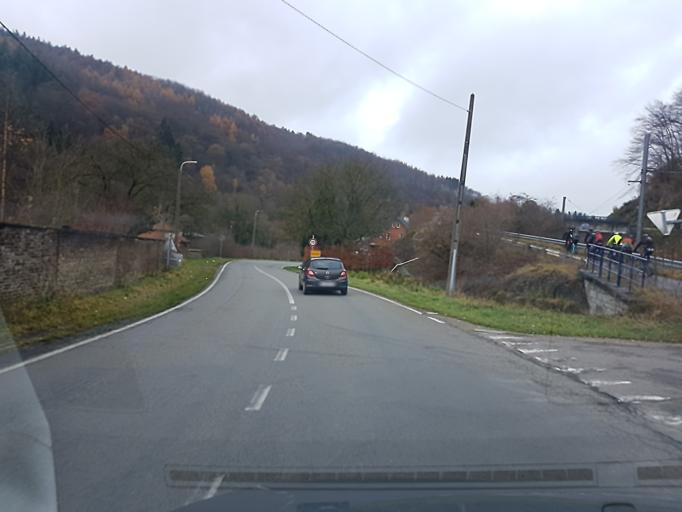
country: BE
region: Wallonia
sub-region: Province de Liege
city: Theux
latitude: 50.5526
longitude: 5.8068
